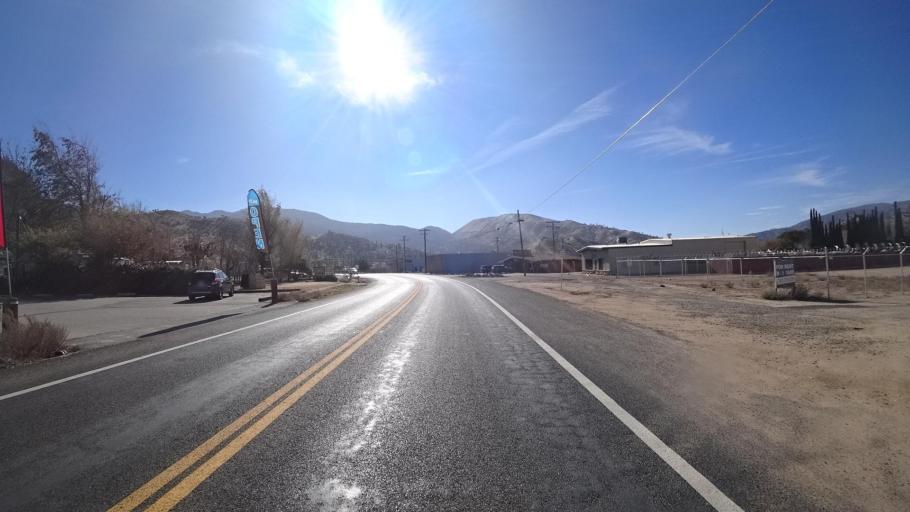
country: US
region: California
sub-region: Kern County
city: Lake Isabella
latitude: 35.6053
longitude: -118.4858
